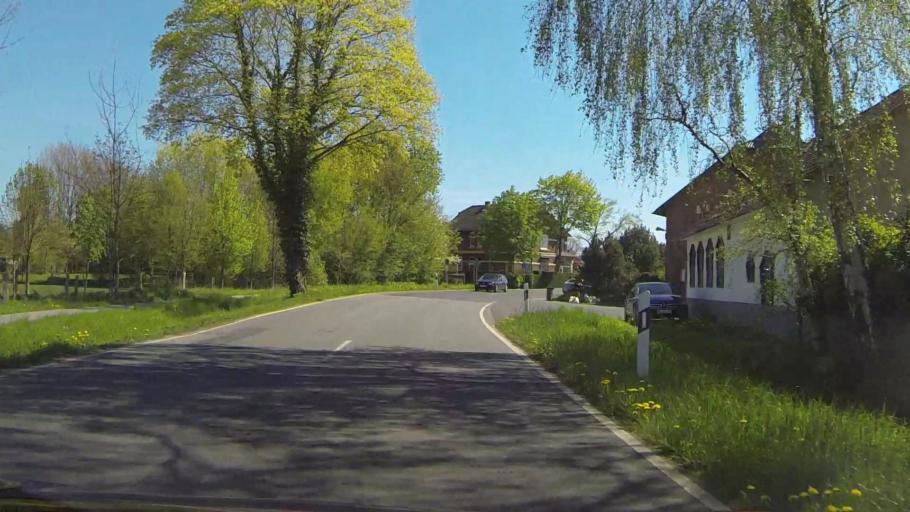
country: DE
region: Schleswig-Holstein
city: Ellerbek
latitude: 53.6490
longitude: 9.8720
